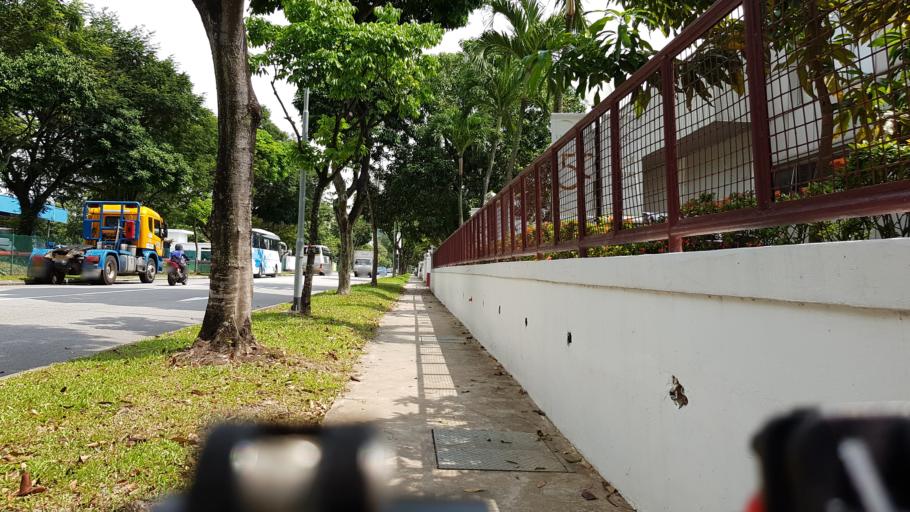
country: MY
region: Johor
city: Kampung Pasir Gudang Baru
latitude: 1.4419
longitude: 103.8363
